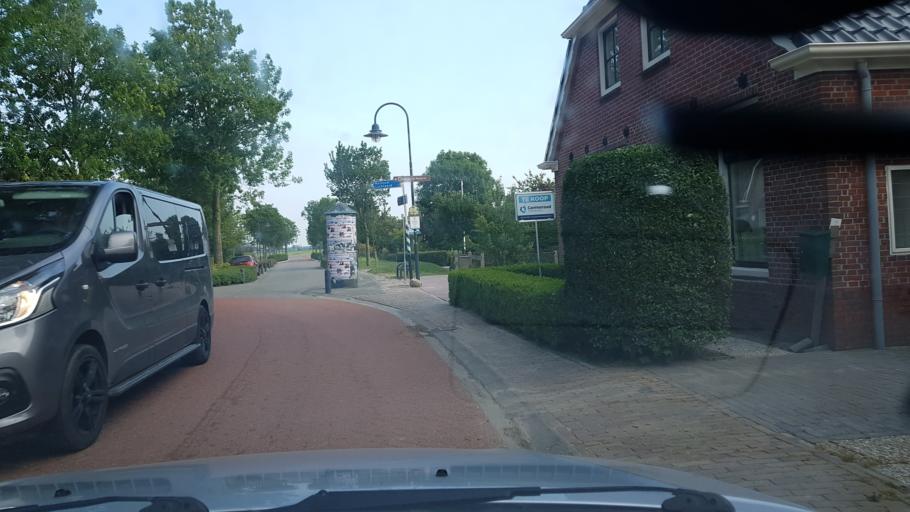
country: NL
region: Friesland
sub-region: Gemeente Ferwerderadiel
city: Burdaard
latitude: 53.3227
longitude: 5.8743
